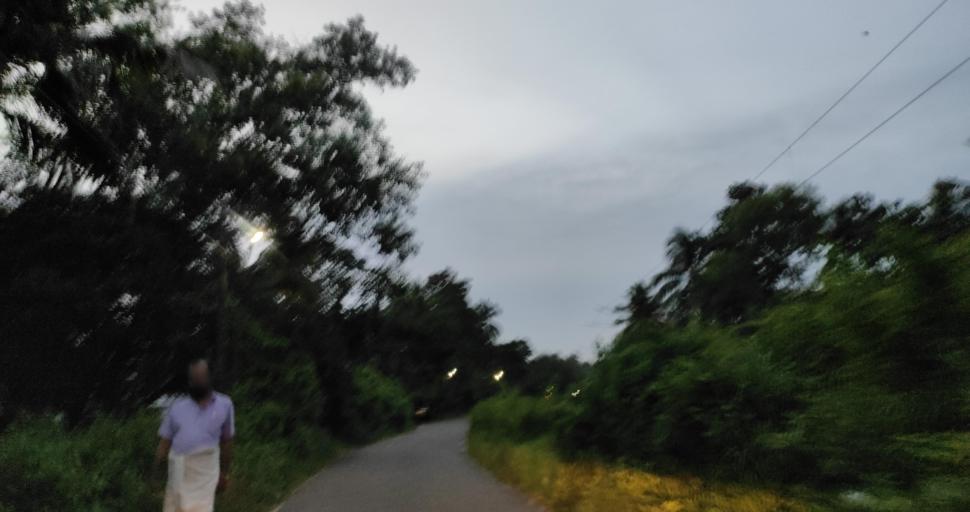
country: IN
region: Kerala
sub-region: Alappuzha
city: Vayalar
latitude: 9.7025
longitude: 76.3132
